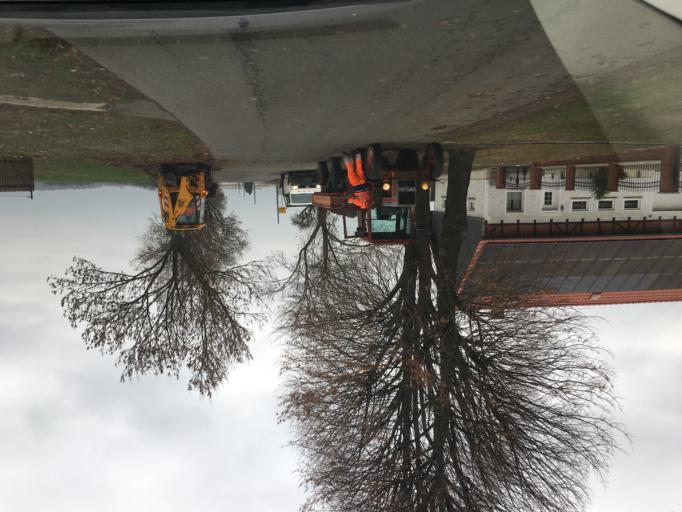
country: DE
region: Saxony-Anhalt
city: Wanzleben
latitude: 52.0391
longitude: 11.4526
